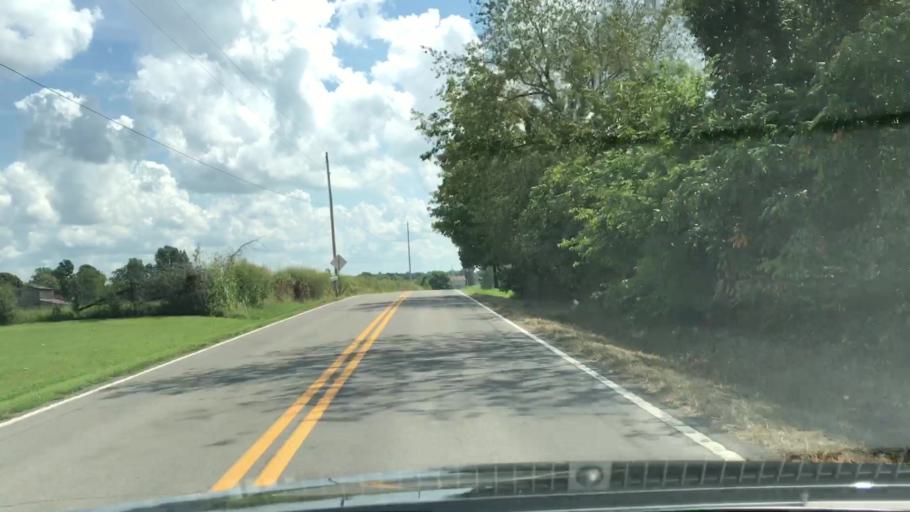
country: US
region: Tennessee
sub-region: Robertson County
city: Springfield
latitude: 36.5995
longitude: -86.9147
